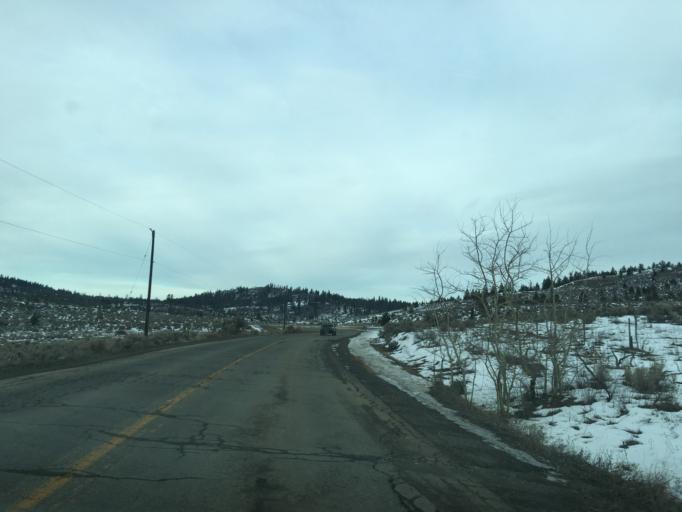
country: CA
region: British Columbia
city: Kamloops
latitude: 50.6263
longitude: -120.4426
